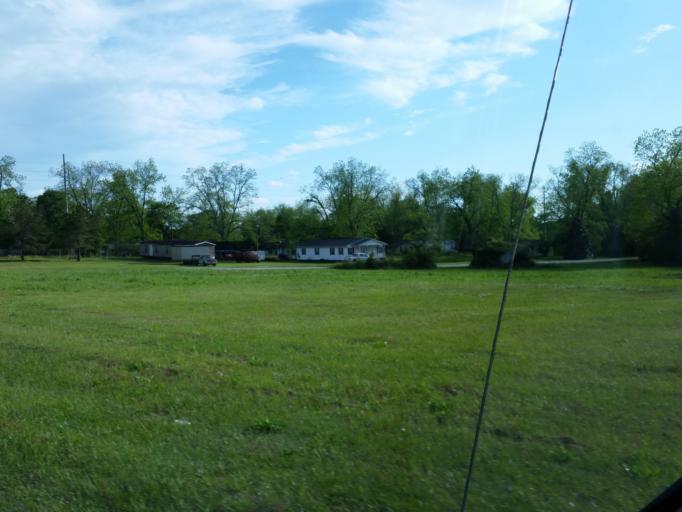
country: US
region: Georgia
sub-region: Crisp County
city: Cordele
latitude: 31.9780
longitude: -83.7885
